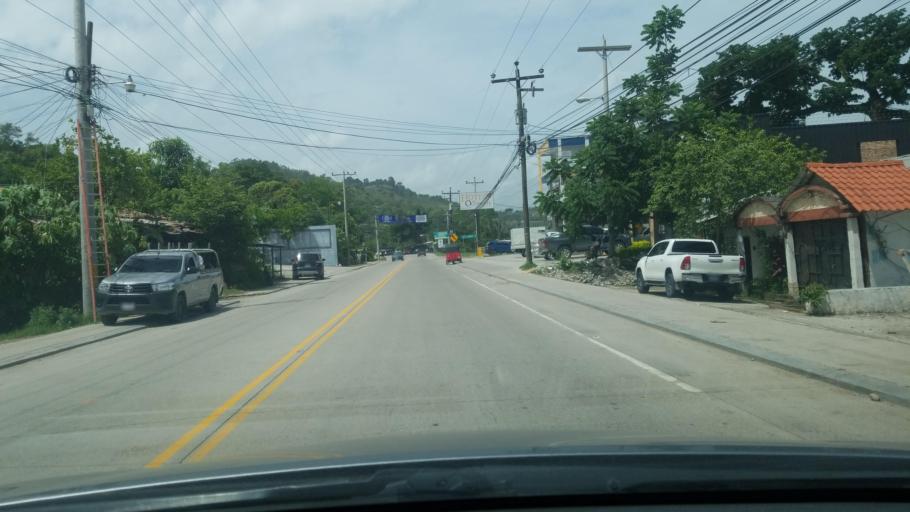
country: HN
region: Copan
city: La Entrada
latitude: 15.0550
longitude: -88.7553
